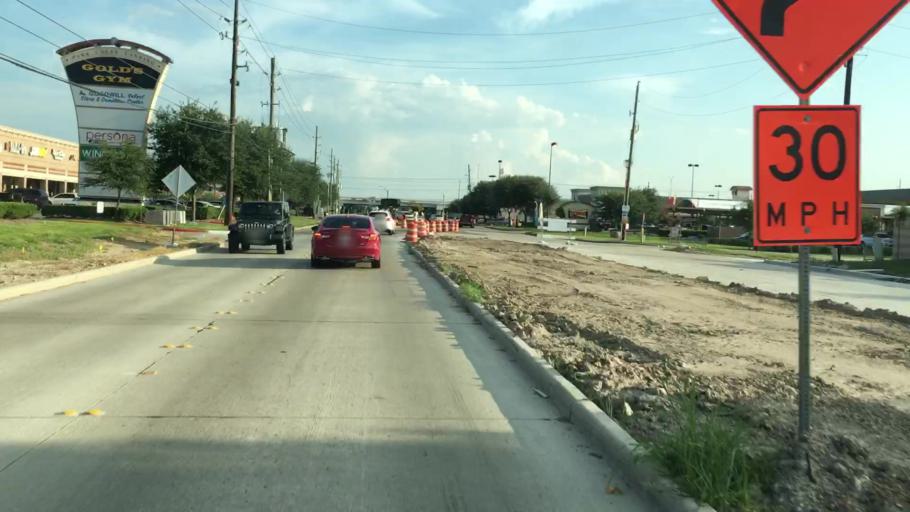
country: US
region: Texas
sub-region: Harris County
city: Humble
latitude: 29.9379
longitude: -95.2495
